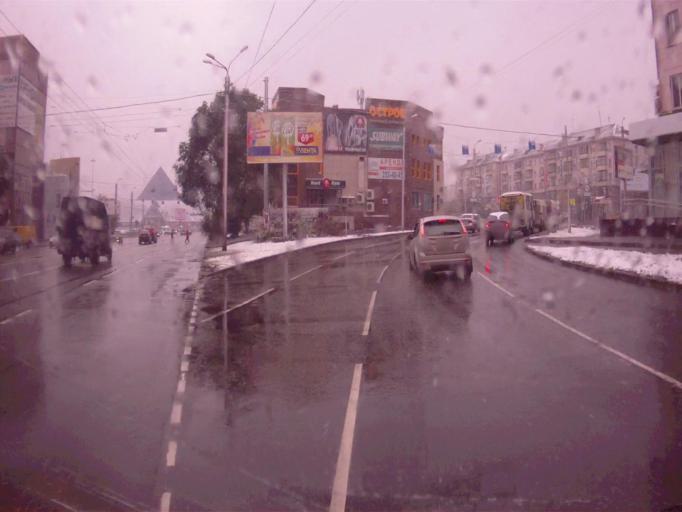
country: RU
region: Chelyabinsk
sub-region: Gorod Chelyabinsk
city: Chelyabinsk
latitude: 55.1439
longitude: 61.4151
